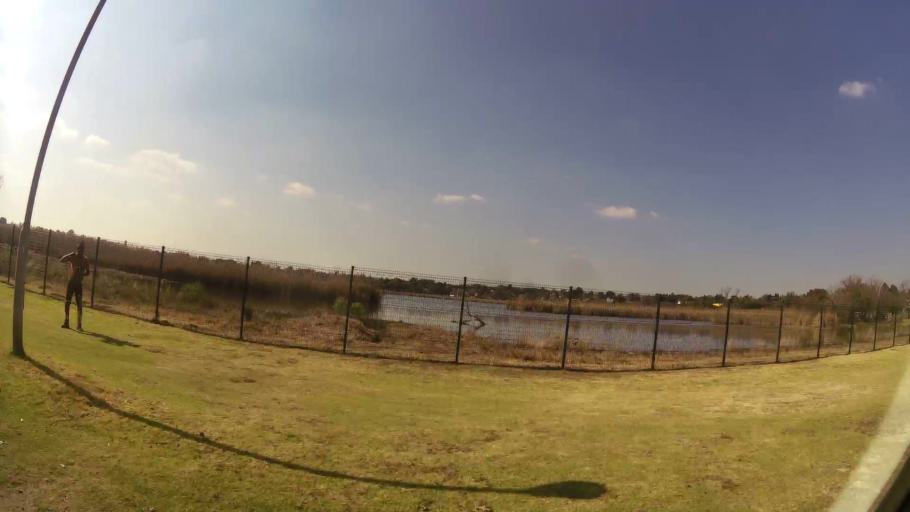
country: ZA
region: Gauteng
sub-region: Ekurhuleni Metropolitan Municipality
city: Benoni
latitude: -26.1945
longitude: 28.2906
